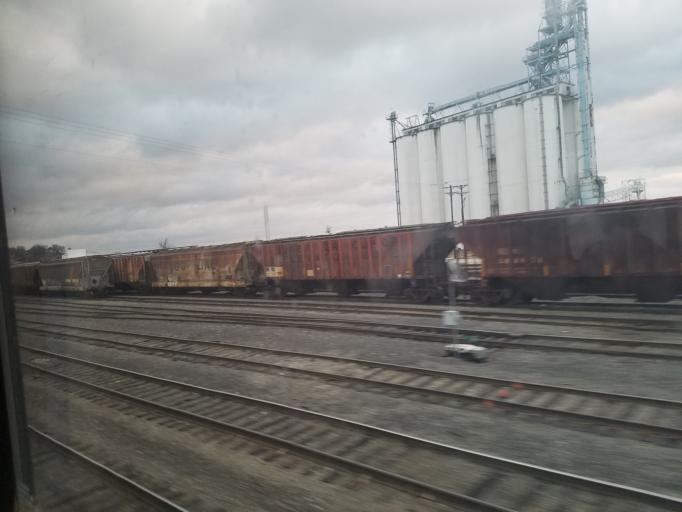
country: US
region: Iowa
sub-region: Des Moines County
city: Burlington
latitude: 40.8106
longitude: -91.0914
